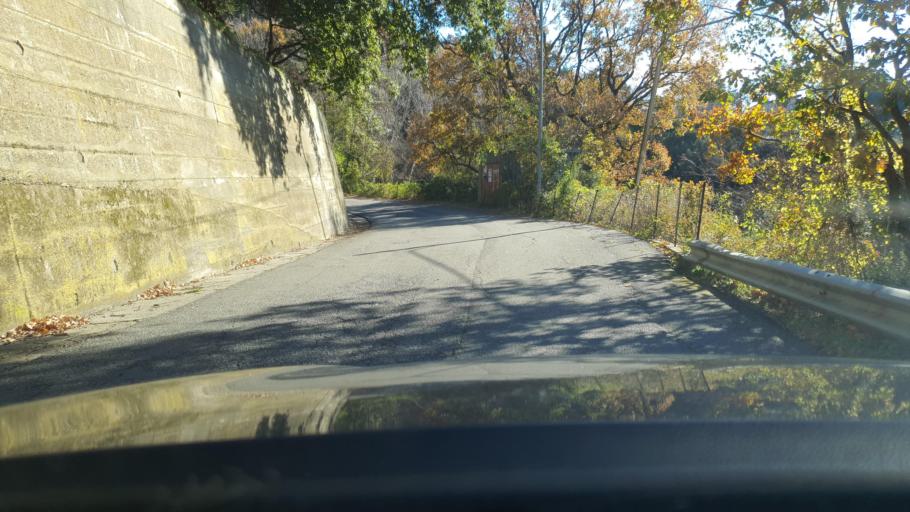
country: IT
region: Calabria
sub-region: Provincia di Catanzaro
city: Sant'Elia
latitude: 38.9618
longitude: 16.5794
